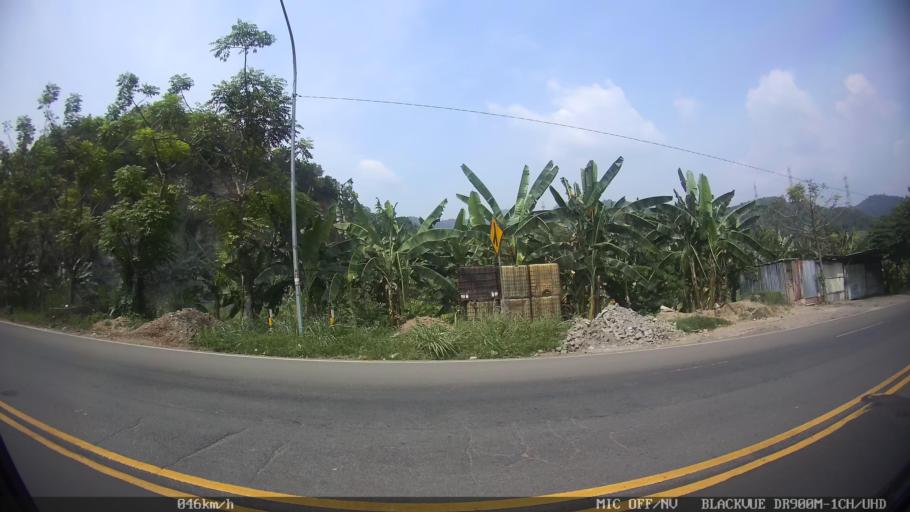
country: ID
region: Banten
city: Curug
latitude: -5.9537
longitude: 106.0023
